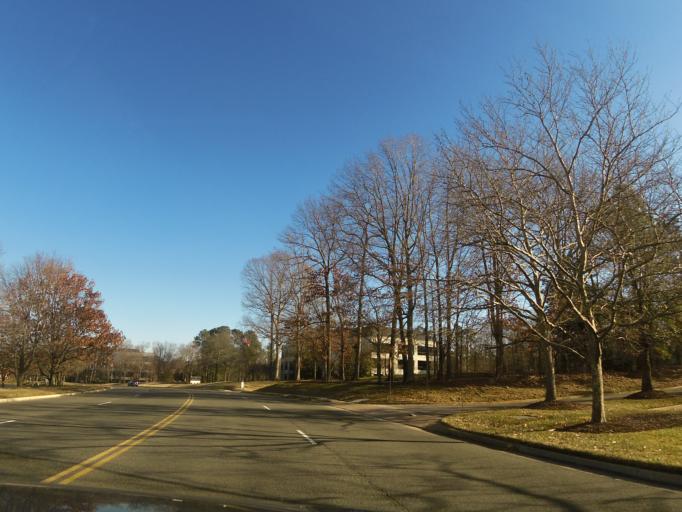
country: US
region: Virginia
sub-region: Henrico County
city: Short Pump
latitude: 37.6583
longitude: -77.5754
